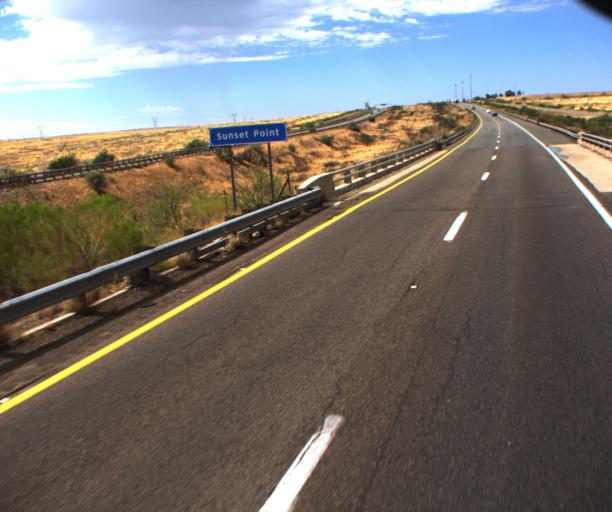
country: US
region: Arizona
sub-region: Yavapai County
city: Cordes Lakes
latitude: 34.1942
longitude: -112.1315
